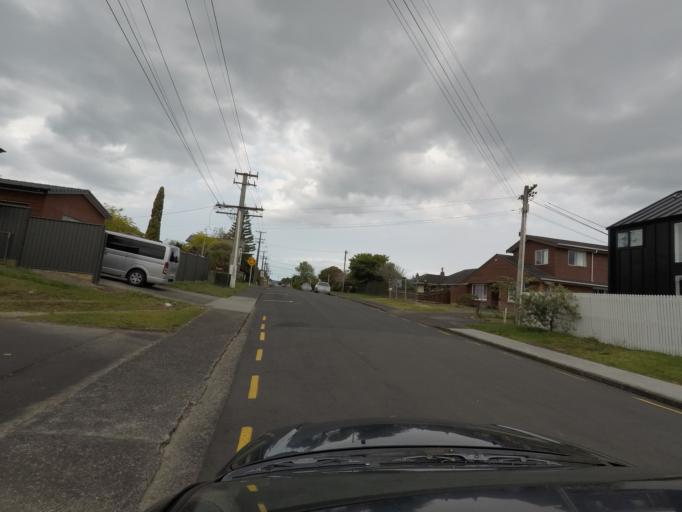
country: NZ
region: Auckland
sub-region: Auckland
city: Rosebank
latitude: -36.8534
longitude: 174.6467
